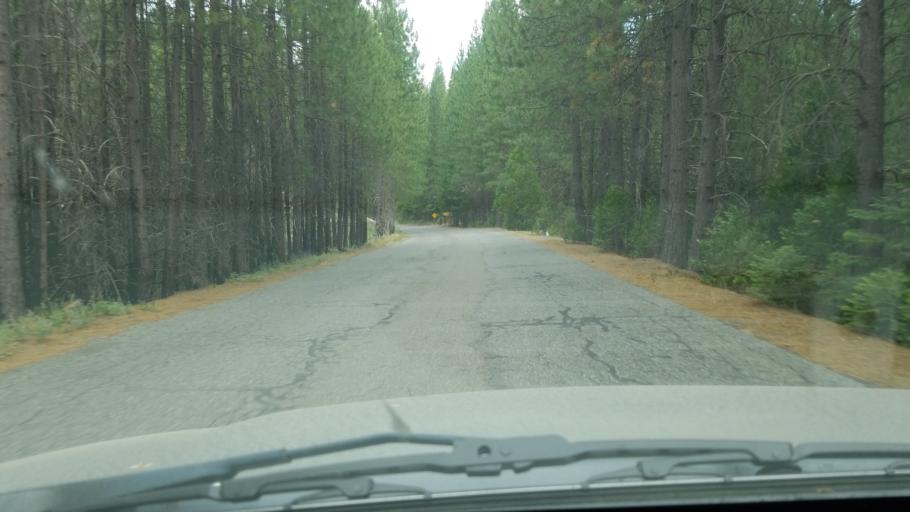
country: US
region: California
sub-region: Mariposa County
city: Midpines
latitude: 37.8160
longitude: -119.8638
